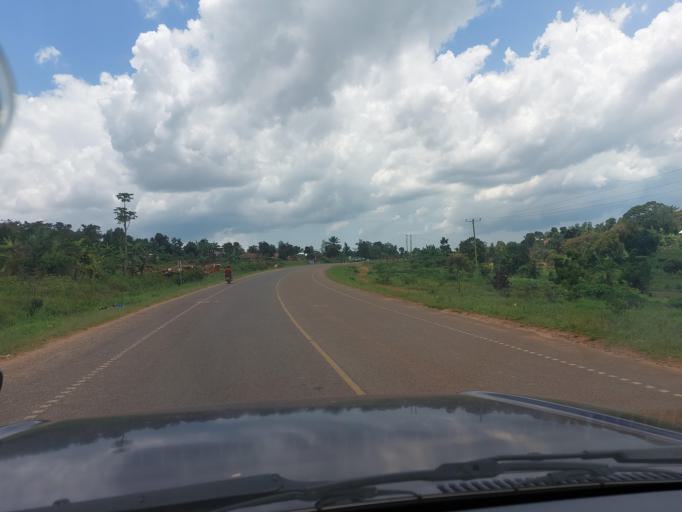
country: UG
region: Central Region
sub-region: Mukono District
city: Mukono
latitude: 0.3099
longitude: 32.7762
